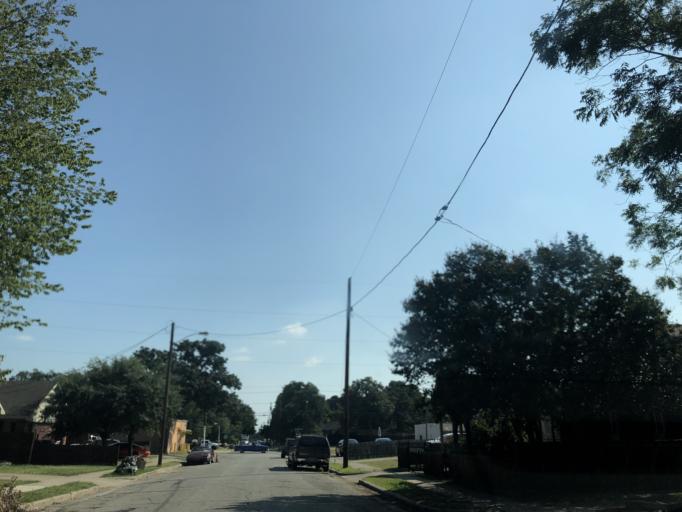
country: US
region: Texas
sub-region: Dallas County
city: Dallas
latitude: 32.7663
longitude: -96.7668
